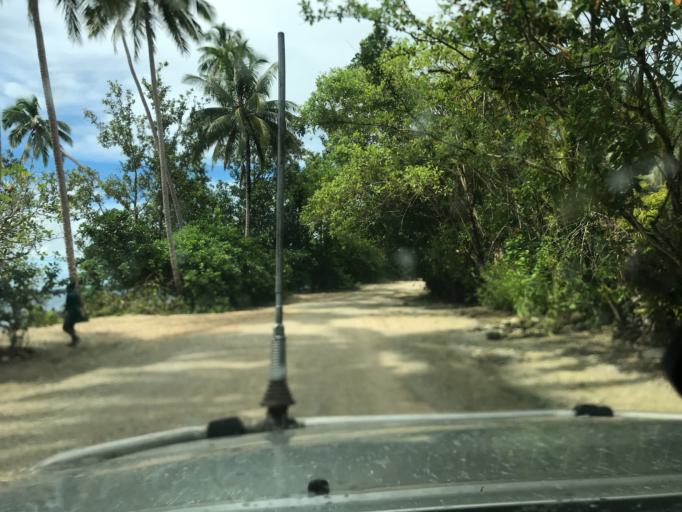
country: SB
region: Malaita
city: Auki
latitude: -8.3637
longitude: 160.6696
